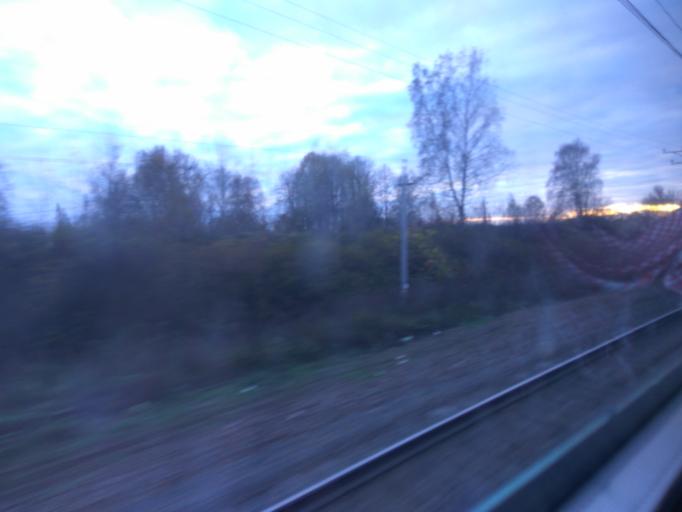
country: RU
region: Moskovskaya
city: Naro-Fominsk
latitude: 55.3834
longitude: 36.7653
